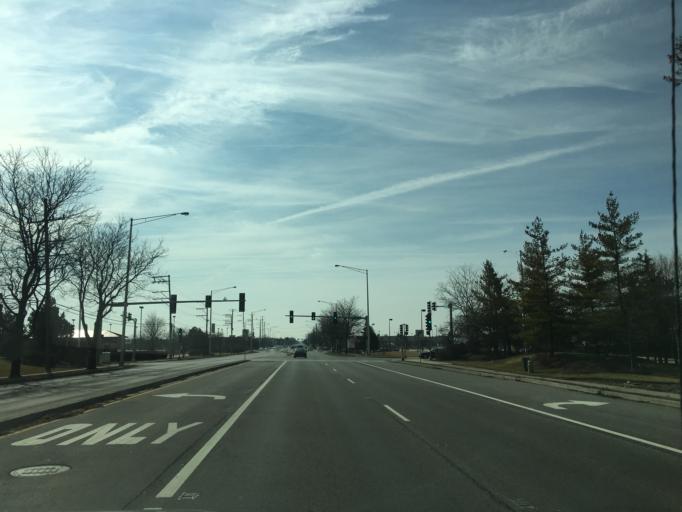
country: US
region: Illinois
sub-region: DuPage County
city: Hanover Park
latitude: 42.0292
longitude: -88.1446
